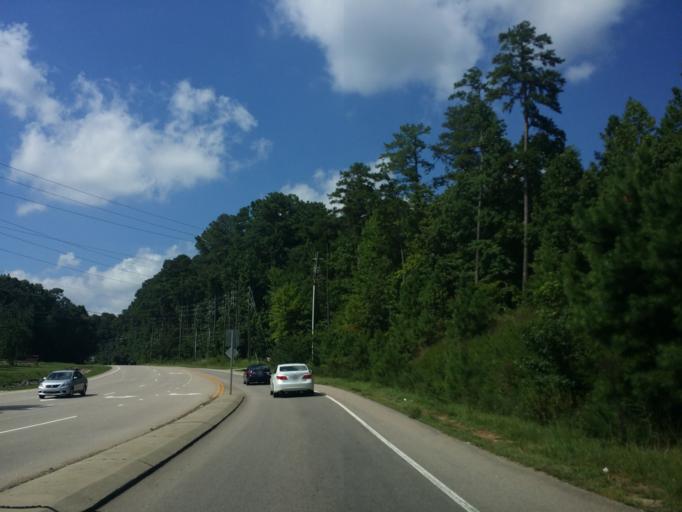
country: US
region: North Carolina
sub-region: Wake County
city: West Raleigh
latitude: 35.8724
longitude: -78.7008
